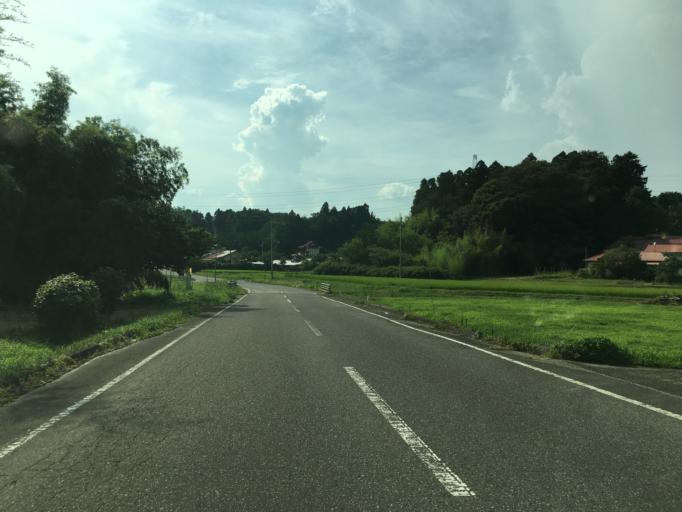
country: JP
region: Fukushima
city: Sukagawa
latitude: 37.3277
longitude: 140.4366
